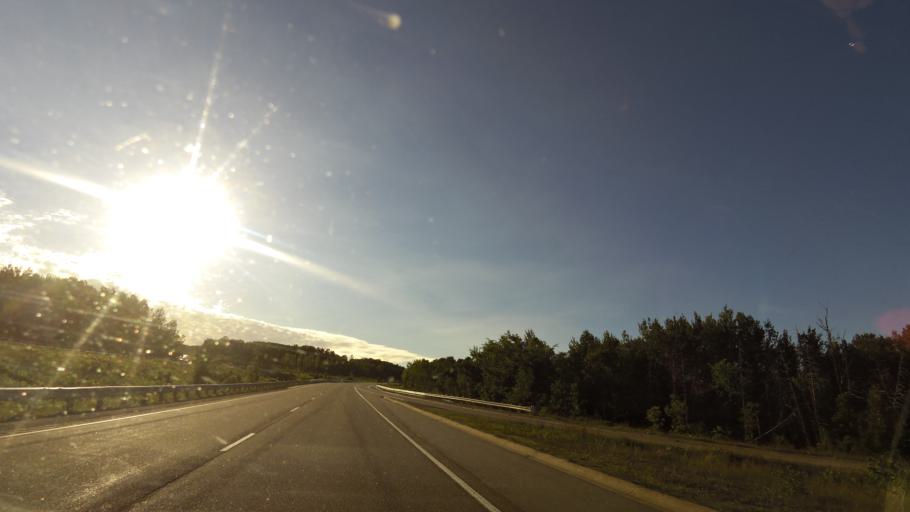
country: CA
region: Ontario
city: Midland
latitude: 44.7048
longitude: -79.6585
